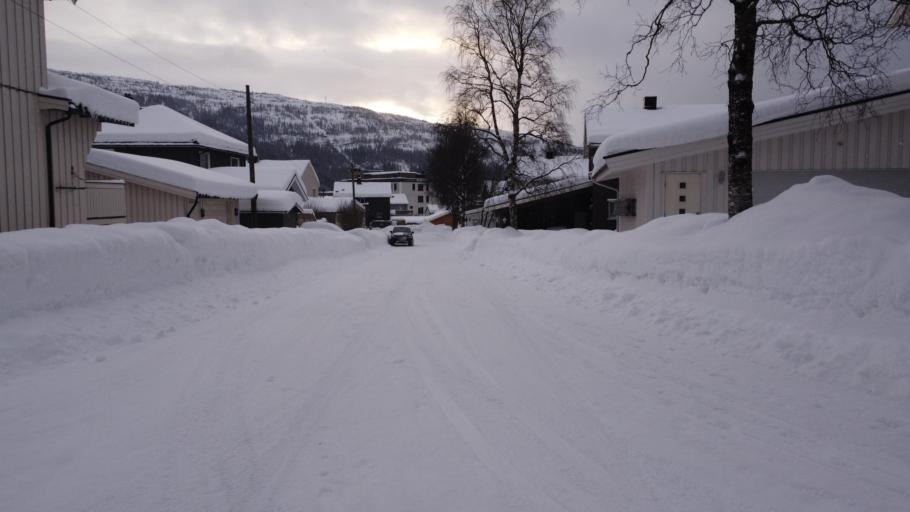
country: NO
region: Nordland
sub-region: Rana
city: Mo i Rana
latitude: 66.3140
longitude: 14.1483
